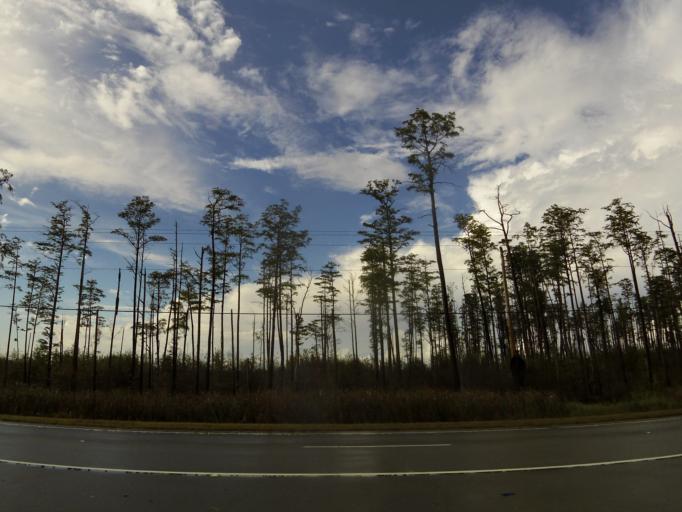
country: US
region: Georgia
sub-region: Long County
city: Ludowici
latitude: 31.7242
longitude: -81.7253
